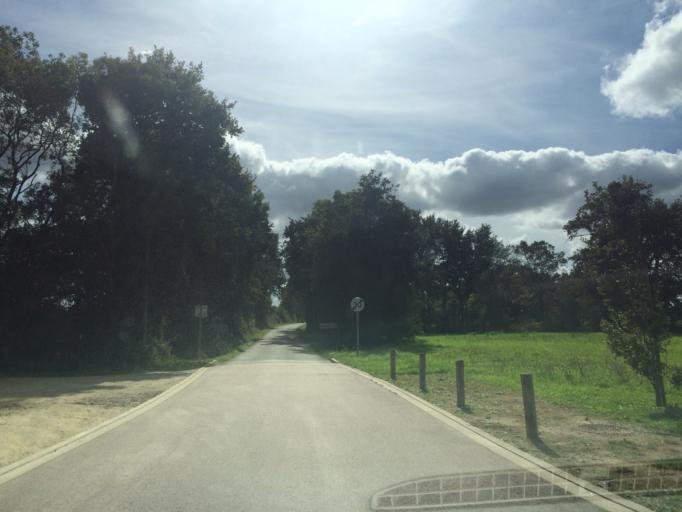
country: FR
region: Pays de la Loire
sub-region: Departement de la Loire-Atlantique
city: Chemere
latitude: 47.1127
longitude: -1.9171
